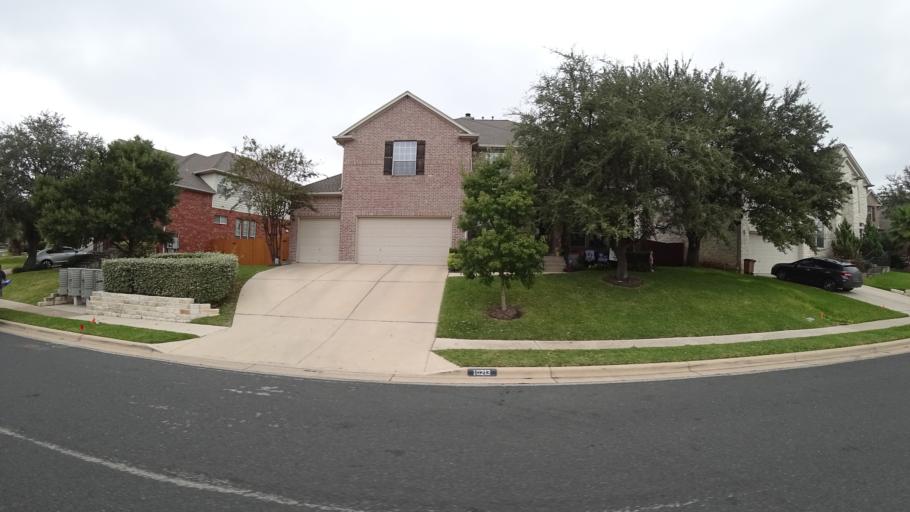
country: US
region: Texas
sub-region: Williamson County
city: Anderson Mill
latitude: 30.4338
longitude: -97.8229
